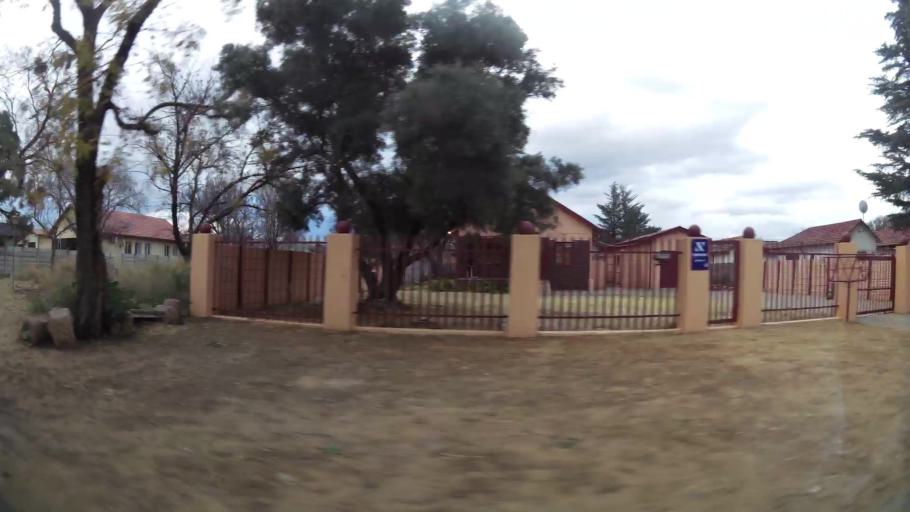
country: ZA
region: Orange Free State
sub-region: Lejweleputswa District Municipality
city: Welkom
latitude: -27.9769
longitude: 26.6985
